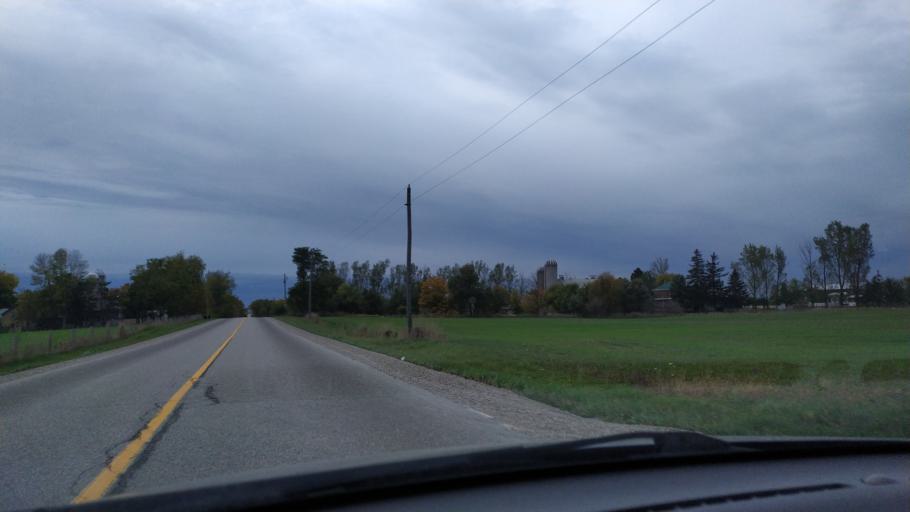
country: CA
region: Ontario
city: Waterloo
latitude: 43.5118
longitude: -80.7337
